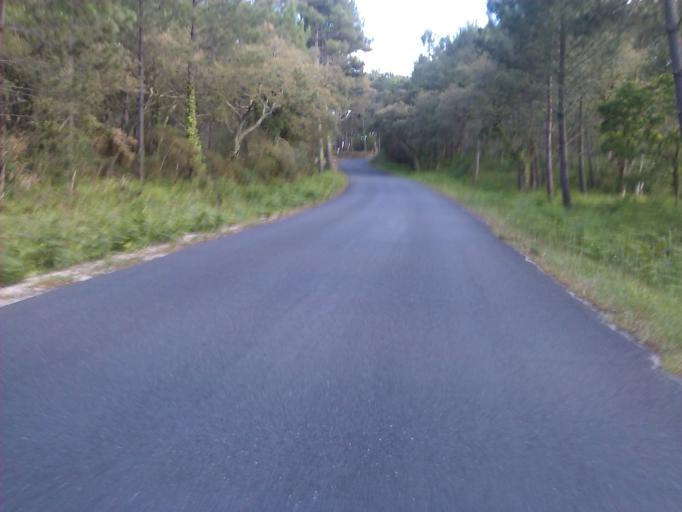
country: FR
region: Aquitaine
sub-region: Departement des Landes
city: Leon
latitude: 43.8702
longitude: -1.3617
